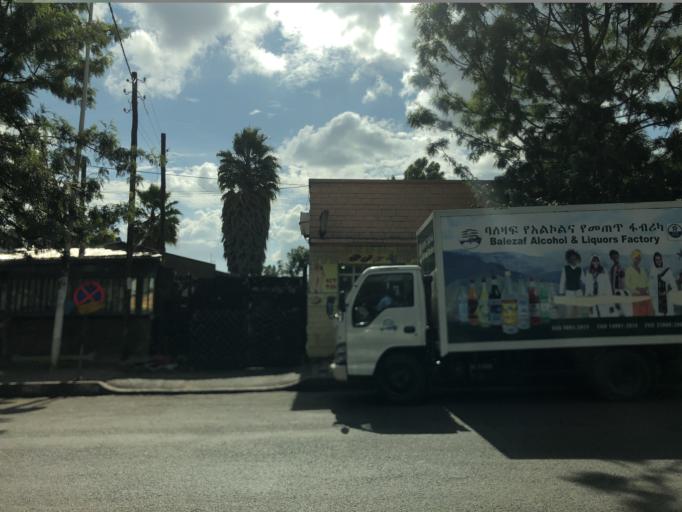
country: ET
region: Adis Abeba
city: Addis Ababa
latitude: 9.0262
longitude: 38.7761
